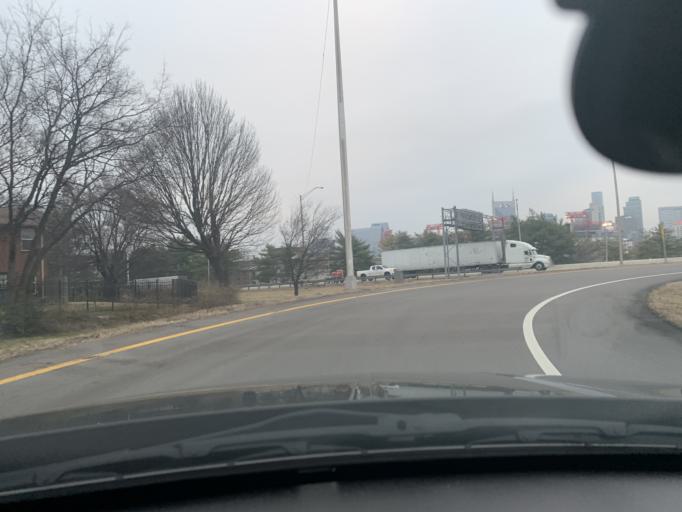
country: US
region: Tennessee
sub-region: Davidson County
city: Nashville
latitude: 36.1702
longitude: -86.7661
